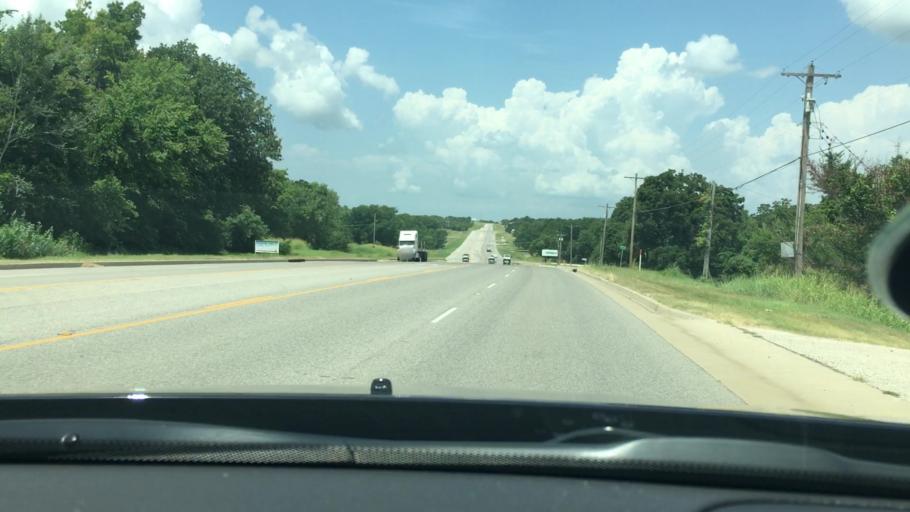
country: US
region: Oklahoma
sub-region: Marshall County
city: Oakland
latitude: 34.1002
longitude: -96.7990
